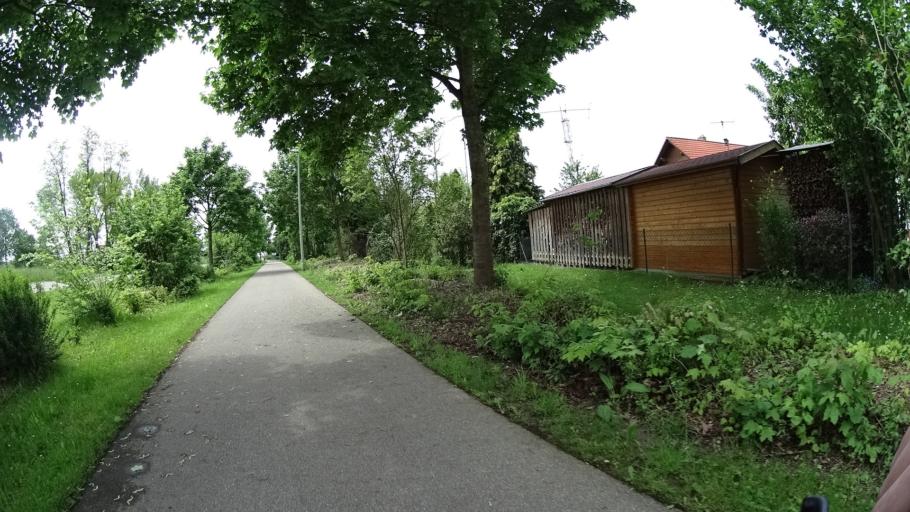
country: DE
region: Bavaria
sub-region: Swabia
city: Pfaffenhofen an der Roth
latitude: 48.3463
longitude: 10.1620
